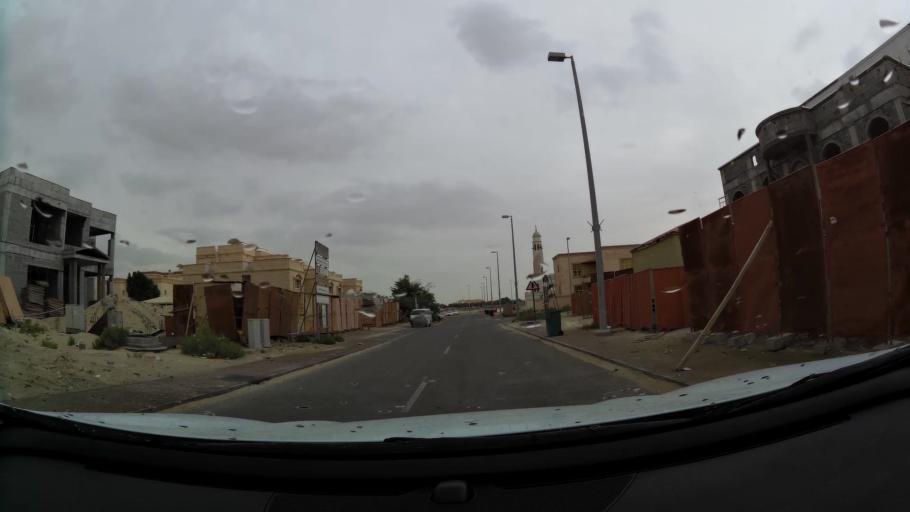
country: AE
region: Abu Dhabi
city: Abu Dhabi
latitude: 24.3700
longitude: 54.6483
